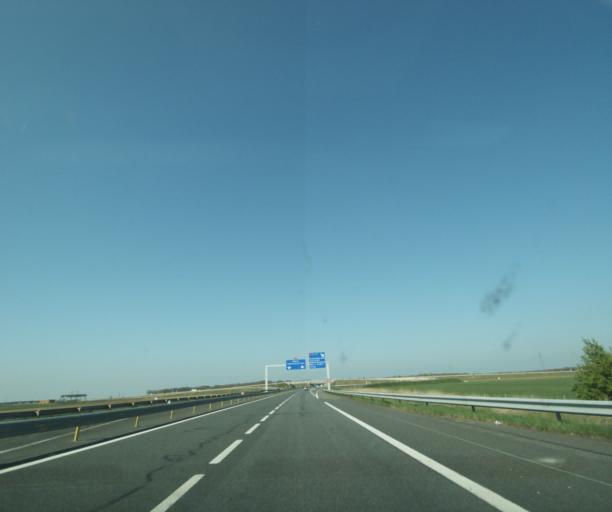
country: FR
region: Centre
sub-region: Departement du Loiret
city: Corquilleroy
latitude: 48.0561
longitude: 2.6708
